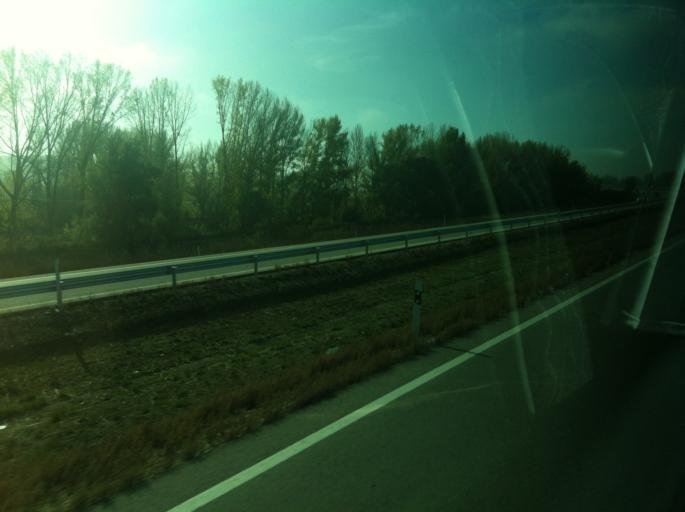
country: ES
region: Castille and Leon
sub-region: Provincia de Burgos
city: Rubena
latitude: 42.3912
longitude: -3.5754
